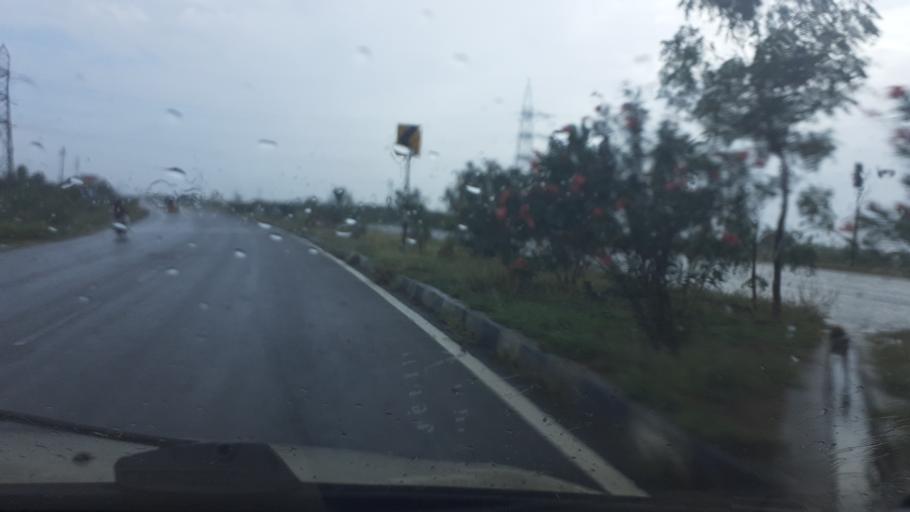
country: IN
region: Tamil Nadu
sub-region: Thoothukkudi
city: Kayattar
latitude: 8.9045
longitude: 77.7639
